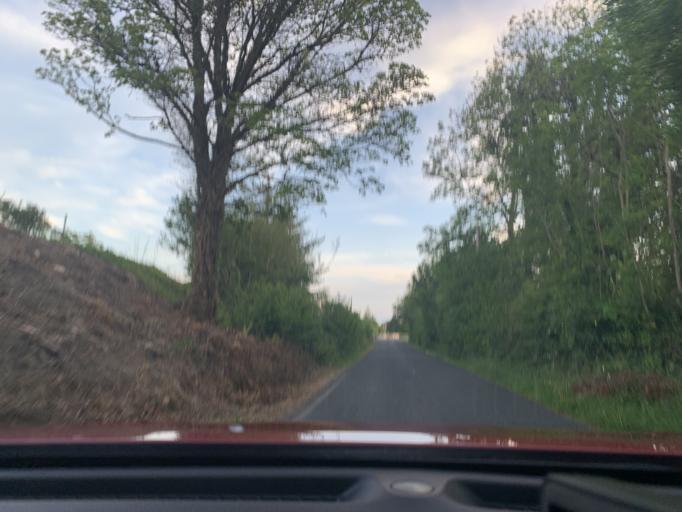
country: IE
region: Connaught
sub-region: Sligo
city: Sligo
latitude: 54.2915
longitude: -8.4442
